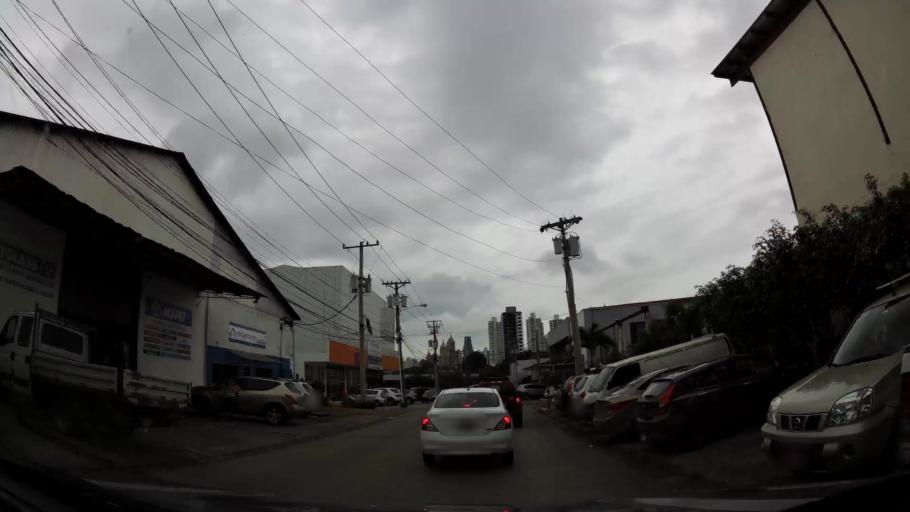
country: PA
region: Panama
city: Panama
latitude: 9.0020
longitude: -79.5279
